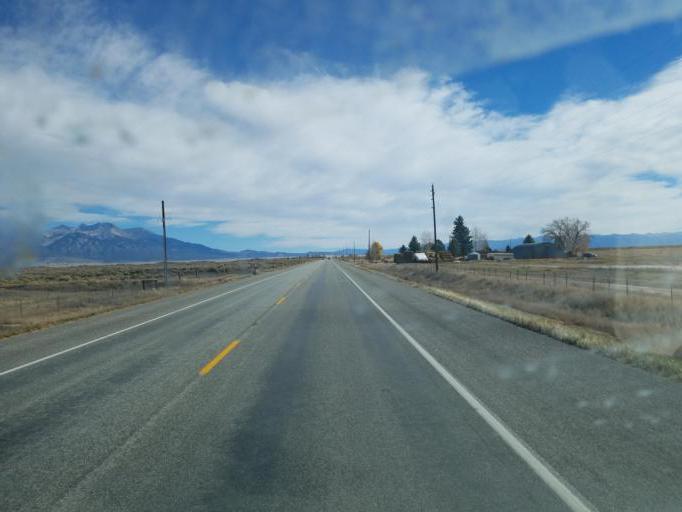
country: US
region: Colorado
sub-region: Alamosa County
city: Alamosa East
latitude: 37.4739
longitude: -105.7592
